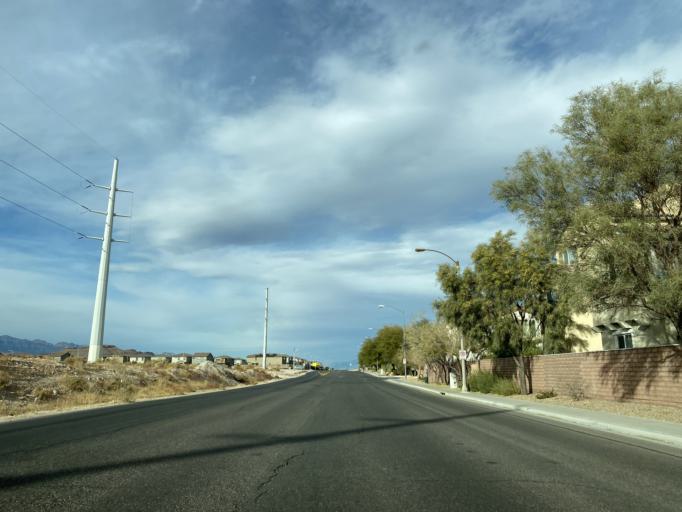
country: US
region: Nevada
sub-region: Clark County
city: Enterprise
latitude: 36.0097
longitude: -115.2982
